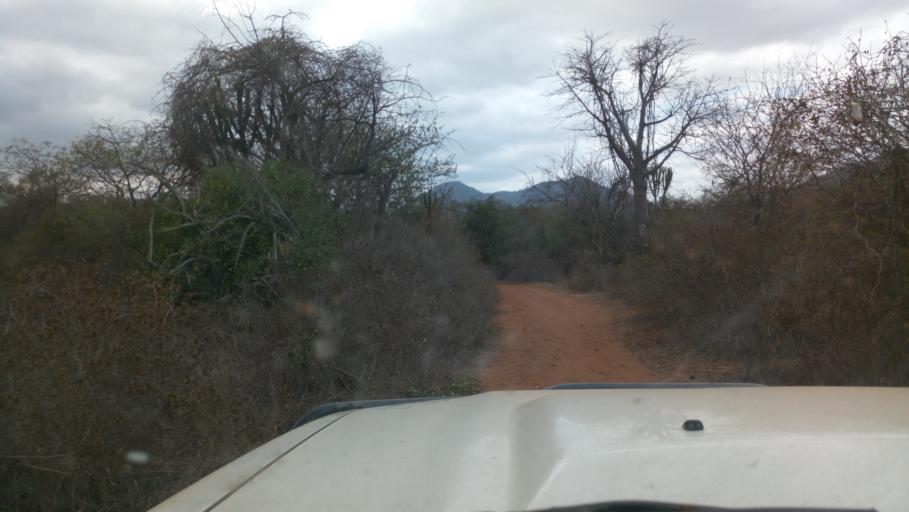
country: KE
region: Kitui
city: Kitui
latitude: -1.8571
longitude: 38.3713
